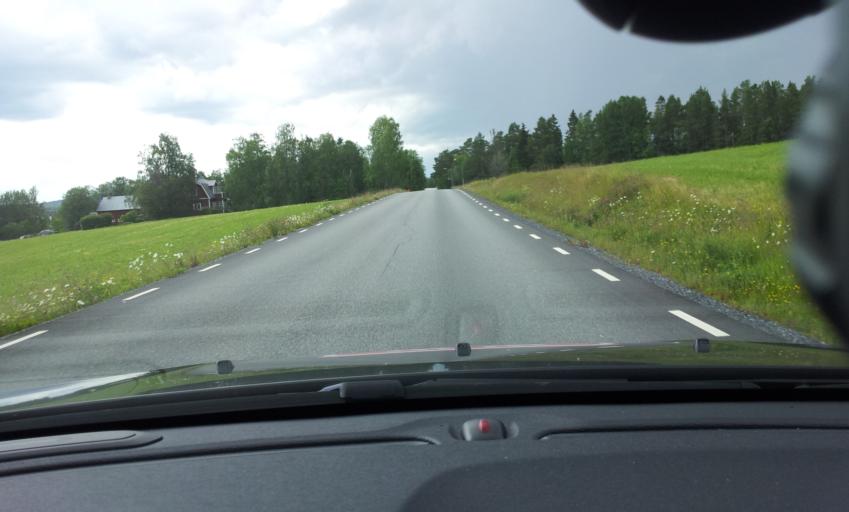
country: SE
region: Jaemtland
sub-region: Krokoms Kommun
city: Valla
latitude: 63.3262
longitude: 14.0353
